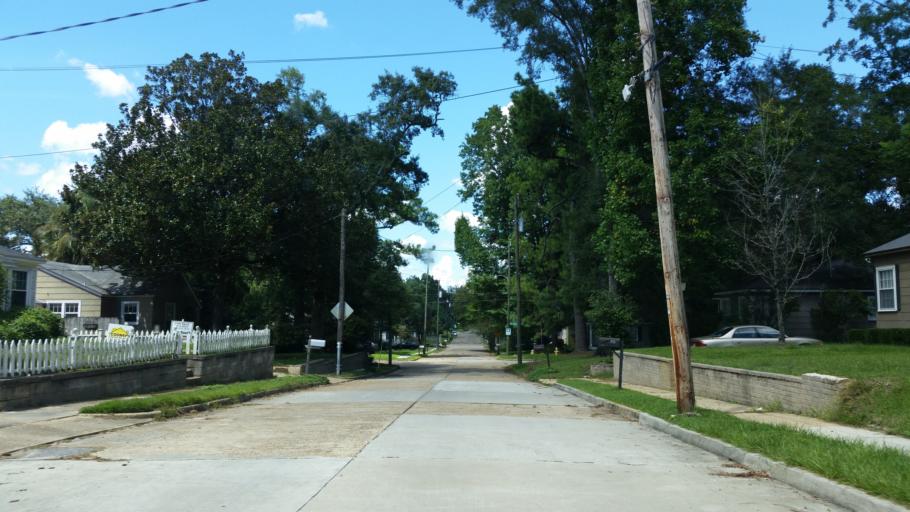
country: US
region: Alabama
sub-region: Mobile County
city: Mobile
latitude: 30.6779
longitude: -88.0967
